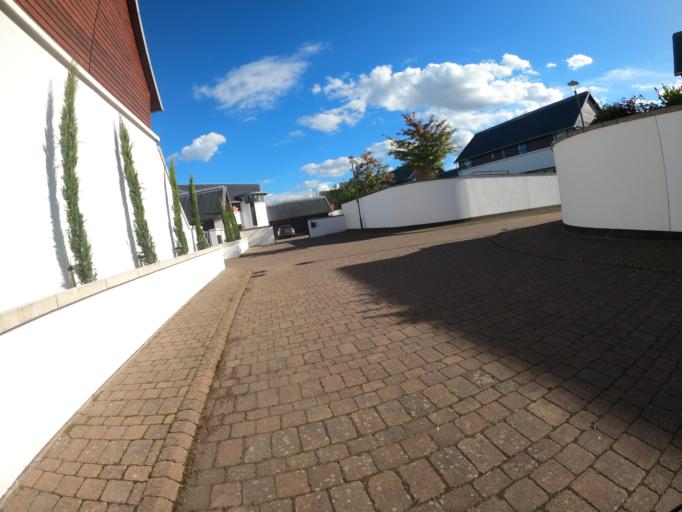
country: GB
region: Scotland
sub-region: Fife
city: Aberdour
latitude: 55.9768
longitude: -3.2943
